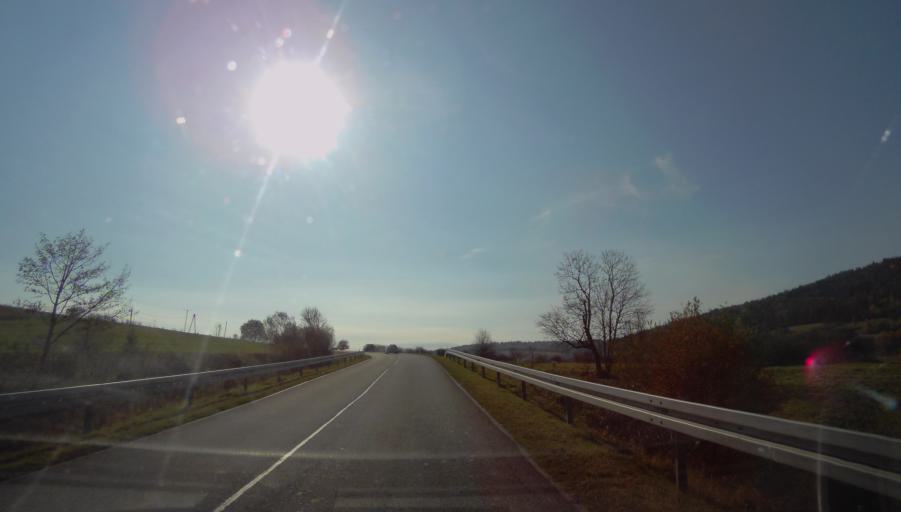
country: PL
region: Subcarpathian Voivodeship
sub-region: Powiat sanocki
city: Komancza
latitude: 49.2779
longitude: 22.0779
